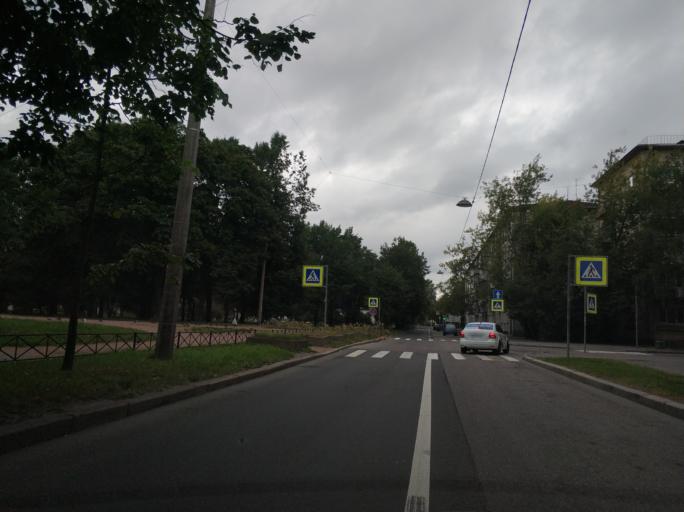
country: RU
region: St.-Petersburg
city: Novaya Derevnya
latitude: 59.9863
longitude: 30.2870
